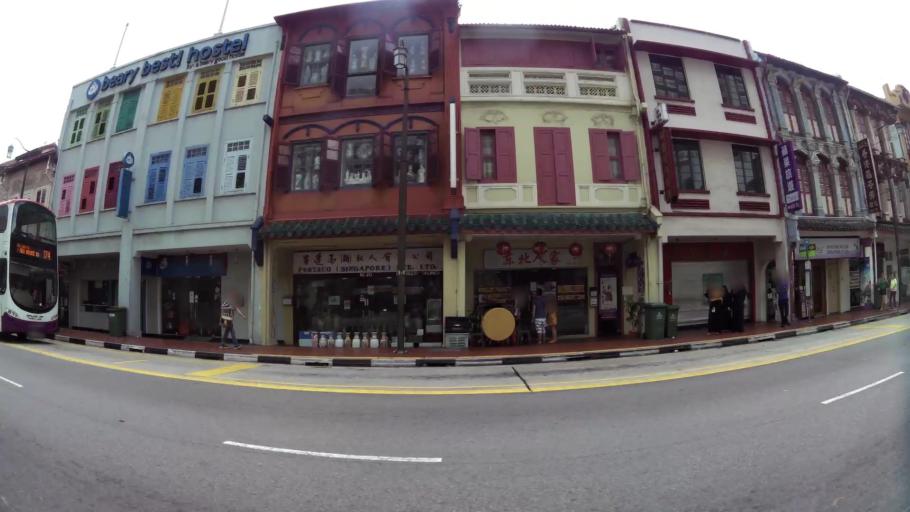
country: SG
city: Singapore
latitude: 1.2841
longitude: 103.8455
